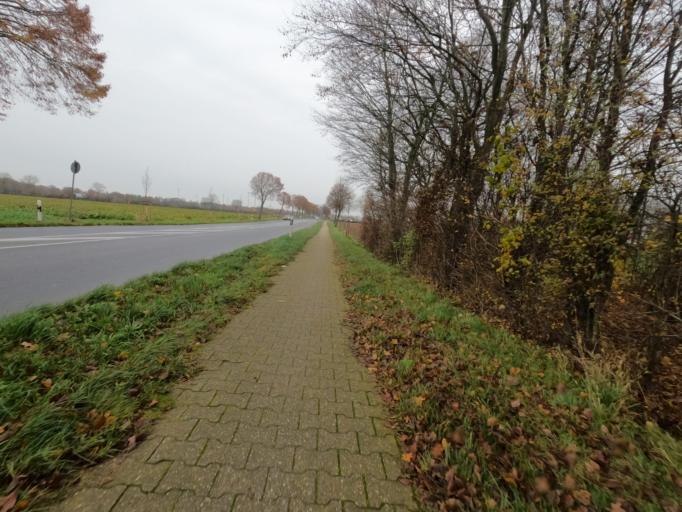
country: DE
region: North Rhine-Westphalia
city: Geilenkirchen
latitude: 50.9942
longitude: 6.1195
